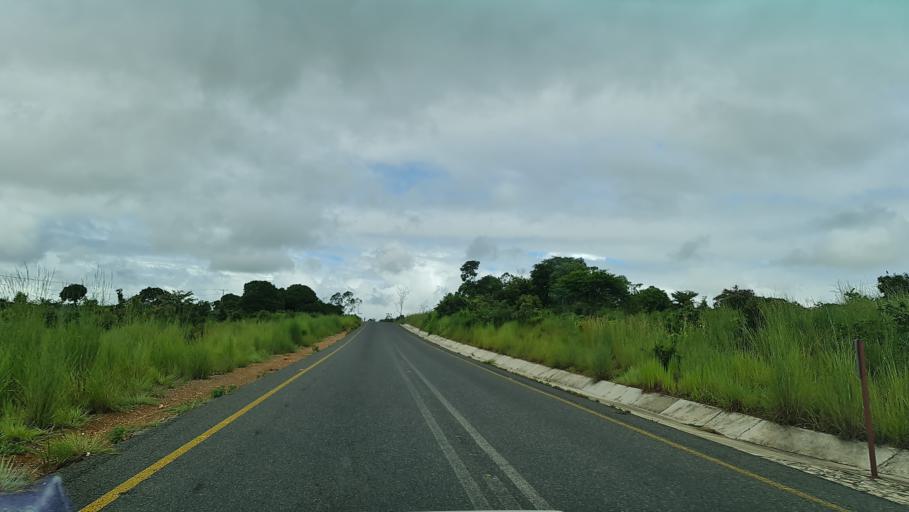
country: MZ
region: Nampula
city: Nampula
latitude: -14.9802
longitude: 38.5241
